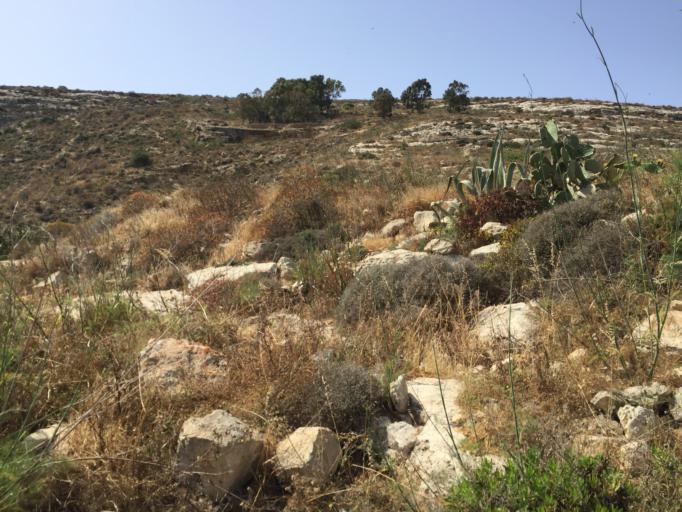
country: MT
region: Saint Lucia
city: Saint Lucia
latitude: 36.0324
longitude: 14.2200
